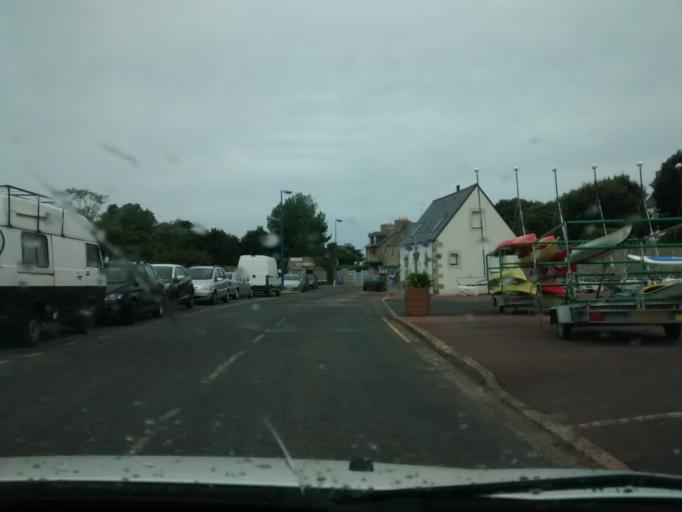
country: FR
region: Brittany
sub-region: Departement des Cotes-d'Armor
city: Trevou-Treguignec
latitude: 48.8365
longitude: -3.3175
